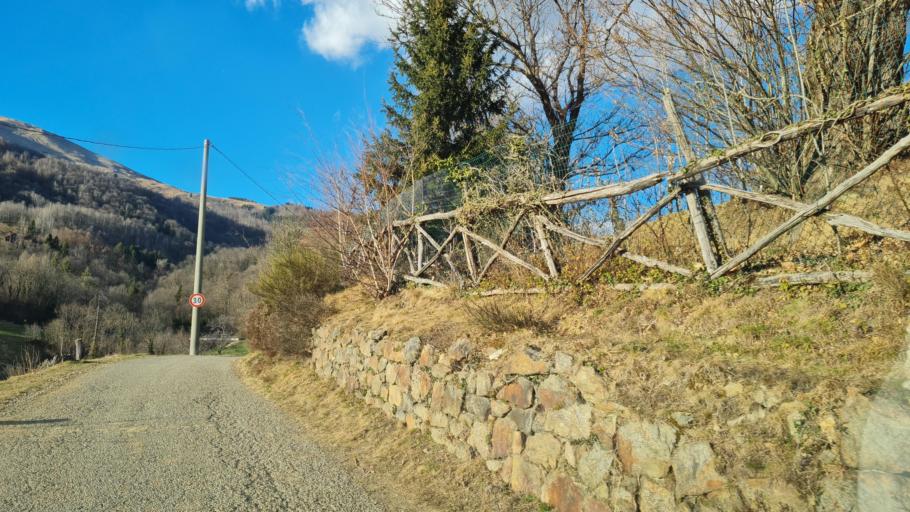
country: IT
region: Piedmont
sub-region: Provincia di Biella
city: Muzzano
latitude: 45.5768
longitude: 7.9896
